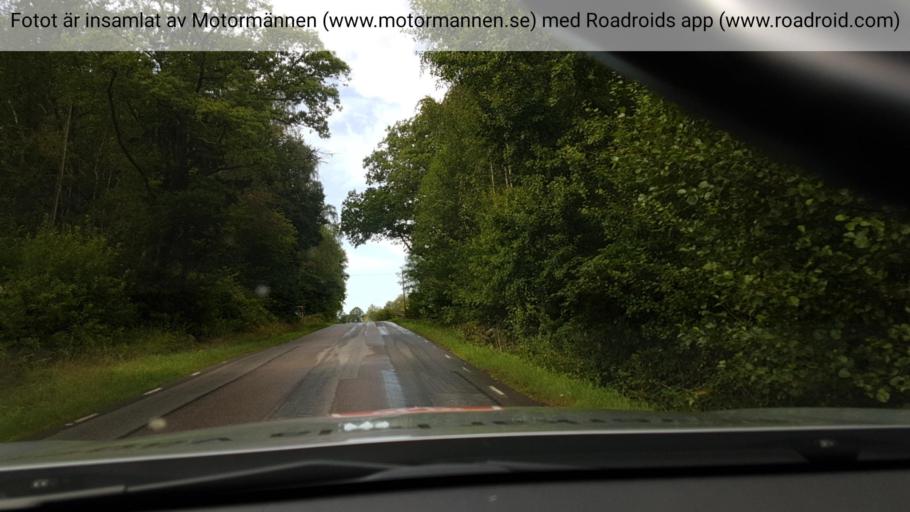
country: SE
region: Vaestra Goetaland
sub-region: Uddevalla Kommun
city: Ljungskile
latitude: 58.2247
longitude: 11.8873
